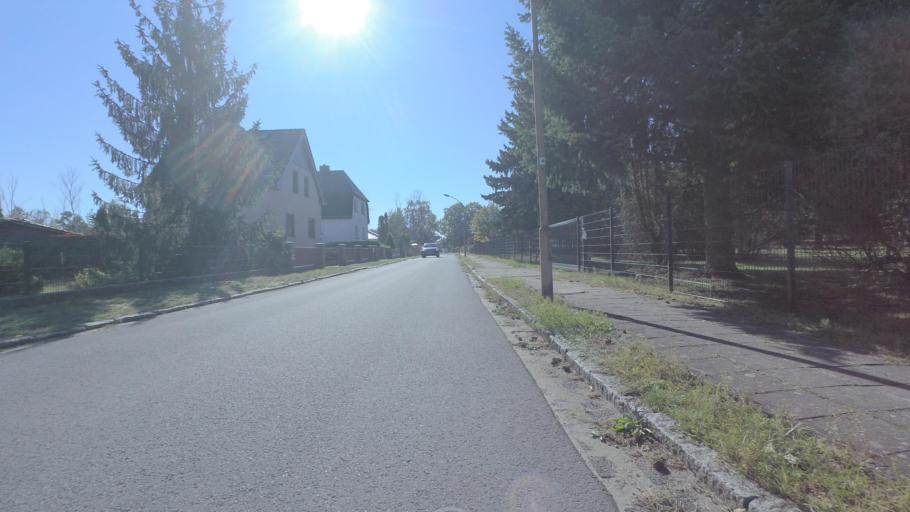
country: DE
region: Brandenburg
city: Sperenberg
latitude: 52.1488
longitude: 13.3693
